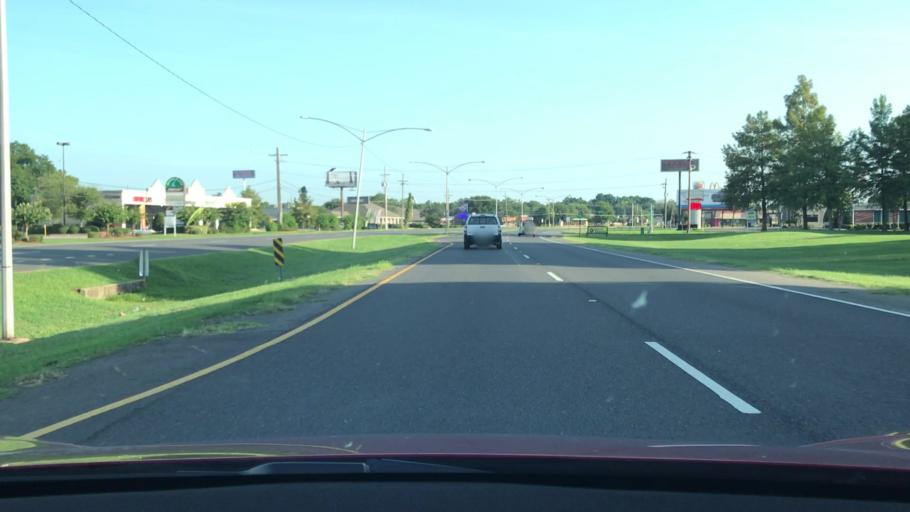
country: US
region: Louisiana
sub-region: Bossier Parish
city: Bossier City
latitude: 32.4477
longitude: -93.7209
